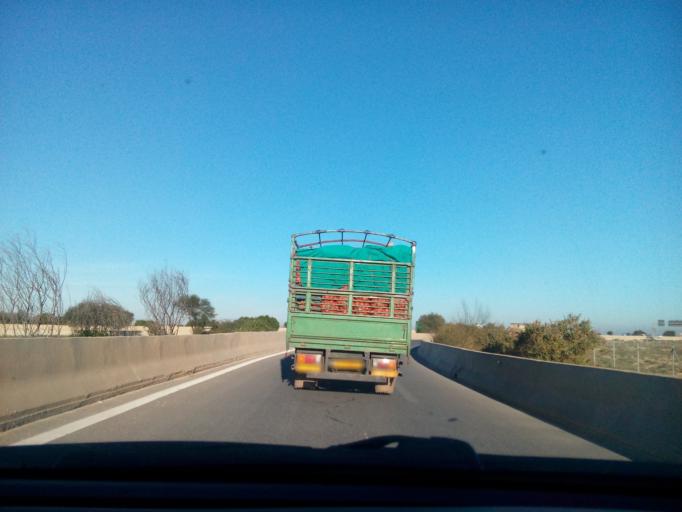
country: DZ
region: Relizane
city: Relizane
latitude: 35.7956
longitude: 0.5373
